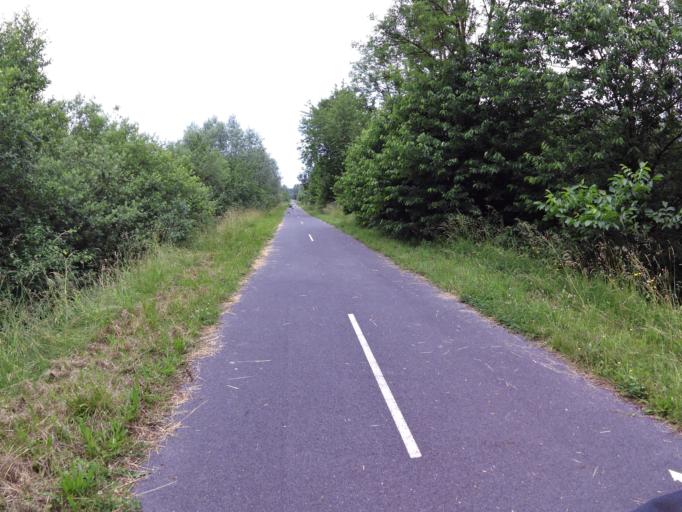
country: FR
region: Champagne-Ardenne
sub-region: Departement des Ardennes
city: Saint-Laurent
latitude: 49.7476
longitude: 4.7739
